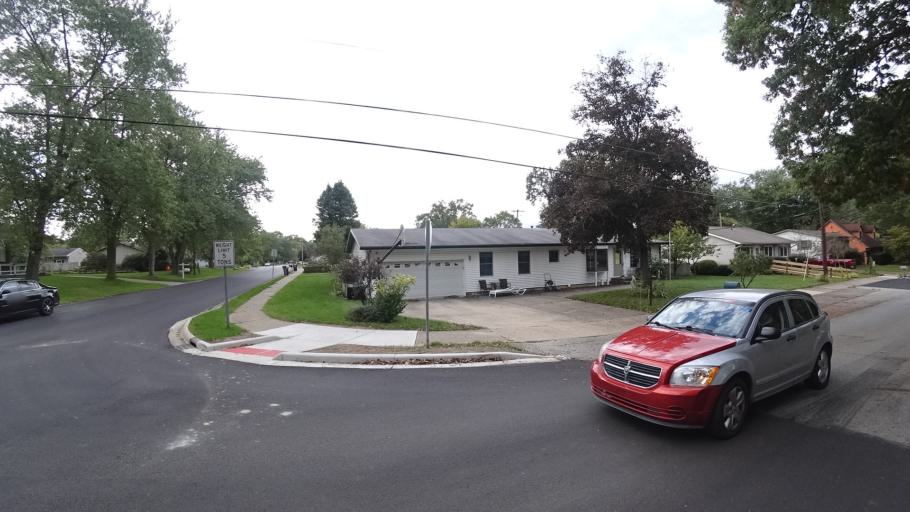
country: US
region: Indiana
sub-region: LaPorte County
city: Trail Creek
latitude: 41.7020
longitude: -86.8648
